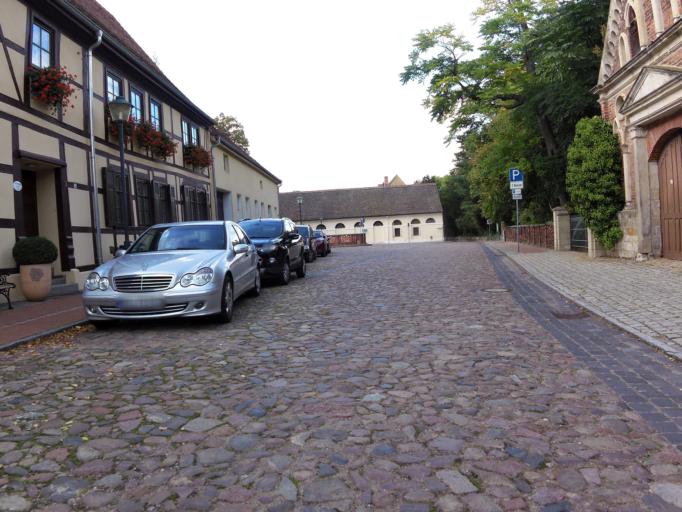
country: DE
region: Saxony-Anhalt
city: Worlitz
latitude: 51.8446
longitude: 12.4213
